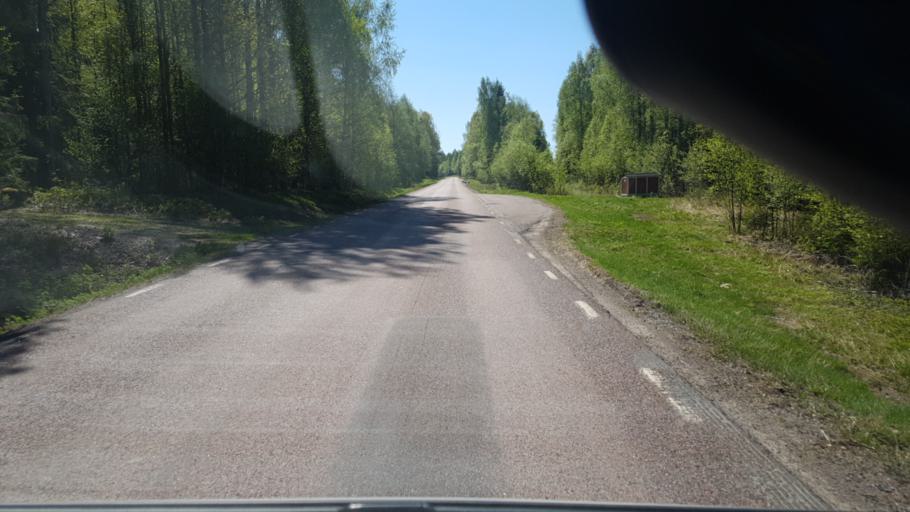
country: SE
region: Vaermland
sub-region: Arvika Kommun
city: Arvika
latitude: 59.9103
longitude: 12.6424
